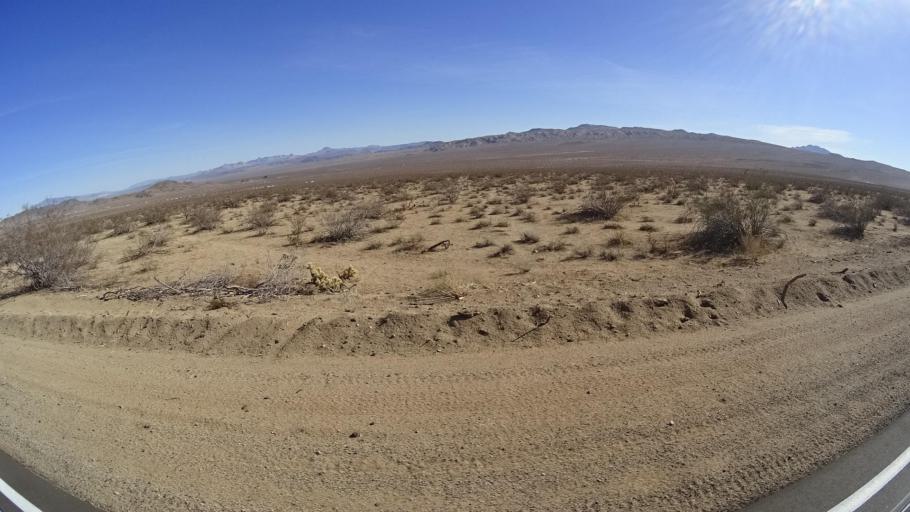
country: US
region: California
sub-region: Kern County
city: Ridgecrest
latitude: 35.5285
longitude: -117.5953
